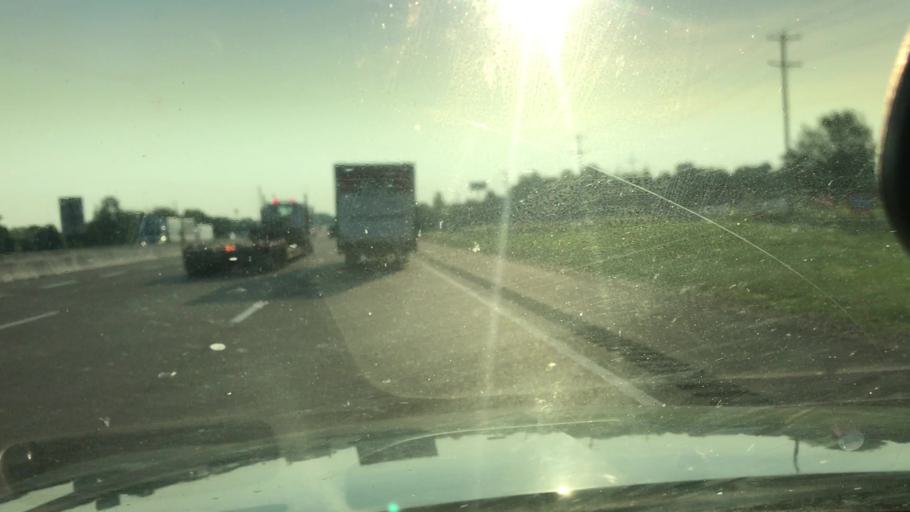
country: US
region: Tennessee
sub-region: Shelby County
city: Bartlett
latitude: 35.1816
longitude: -89.8214
